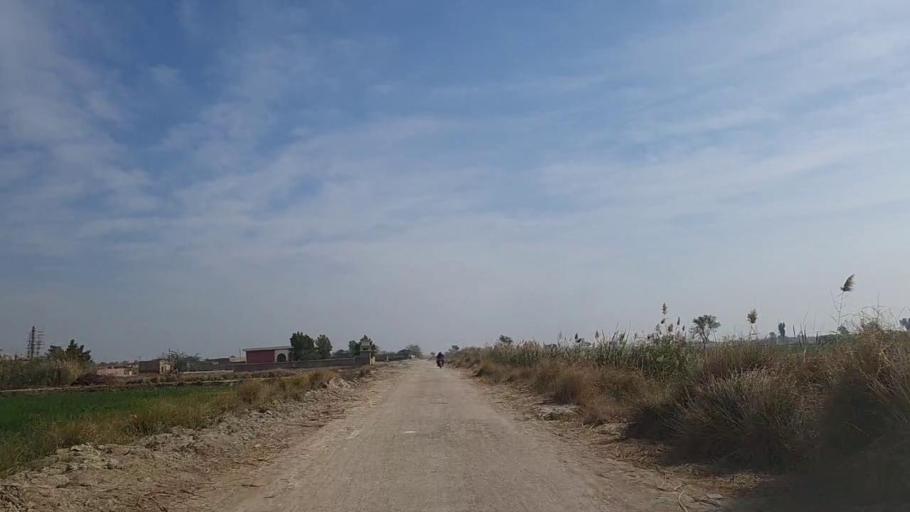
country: PK
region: Sindh
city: Nawabshah
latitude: 26.3320
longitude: 68.4448
